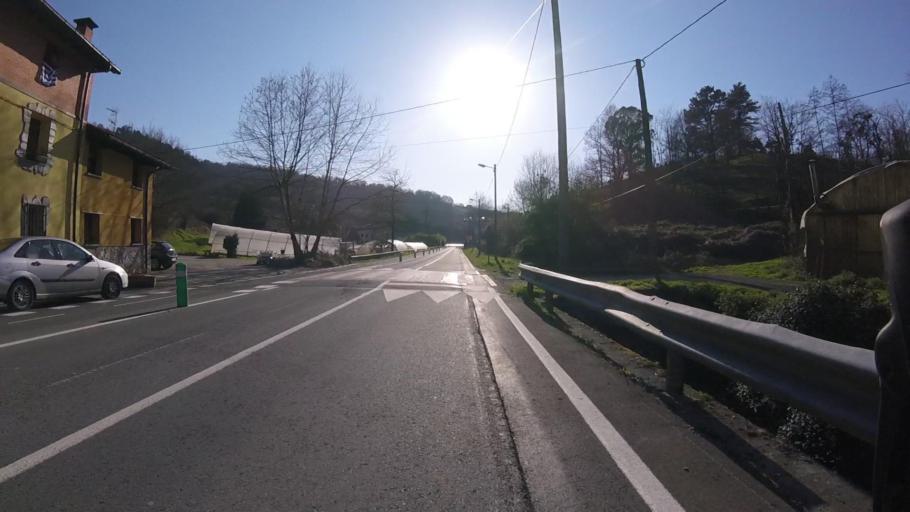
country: ES
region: Basque Country
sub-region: Provincia de Guipuzcoa
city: Astigarraga
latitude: 43.2853
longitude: -1.9369
